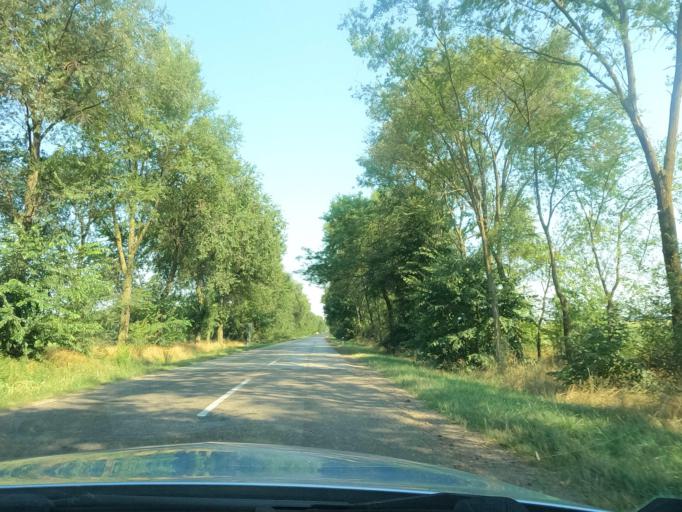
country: RS
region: Autonomna Pokrajina Vojvodina
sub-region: Juznobacki Okrug
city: Becej
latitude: 45.6667
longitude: 19.9349
